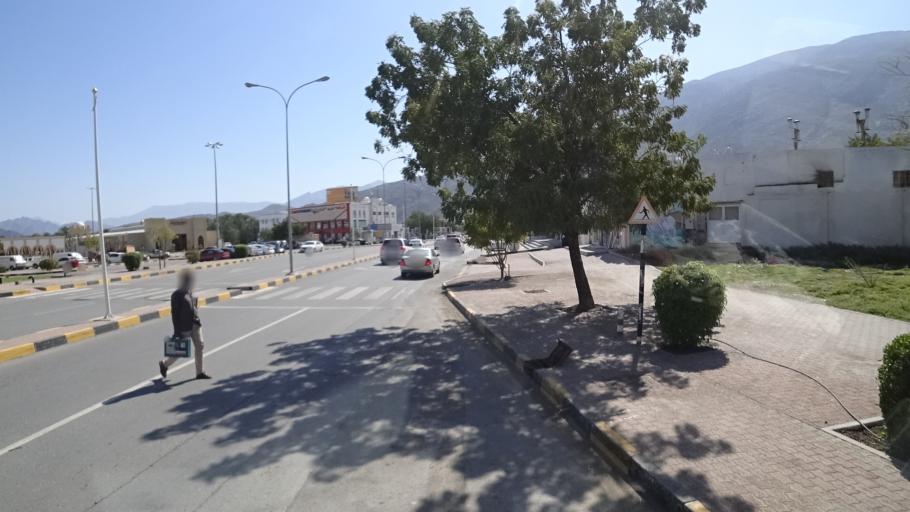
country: OM
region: Al Batinah
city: Rustaq
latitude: 23.3956
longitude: 57.4221
